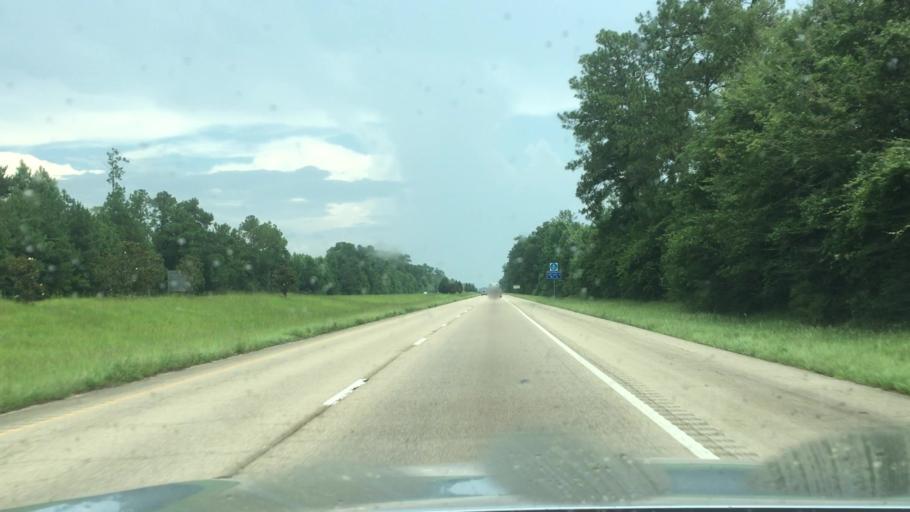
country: US
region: Mississippi
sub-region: Lamar County
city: Lumberton
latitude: 31.0156
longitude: -89.4110
